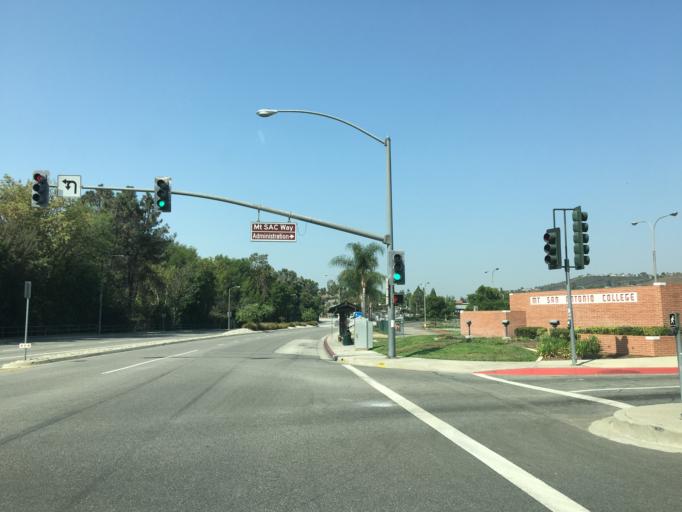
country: US
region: California
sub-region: Los Angeles County
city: Walnut
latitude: 34.0441
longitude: -117.8448
